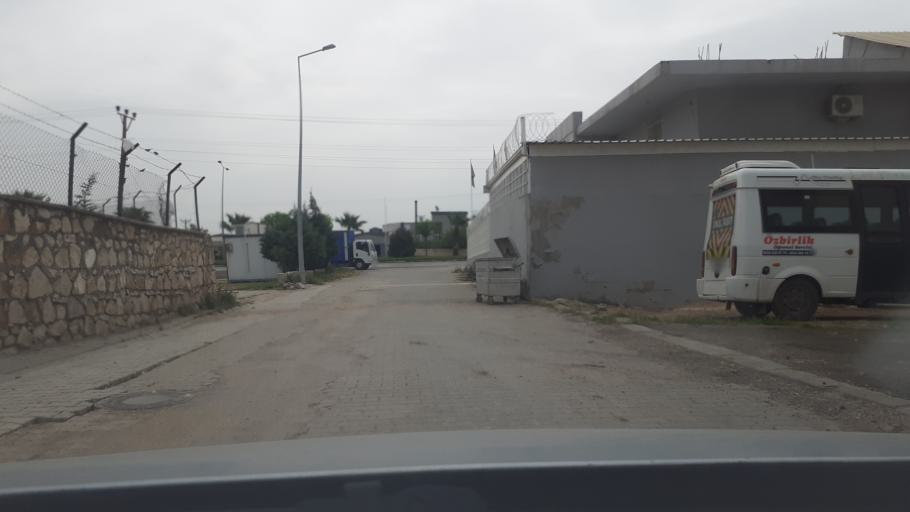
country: TR
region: Hatay
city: Kirikhan
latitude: 36.4916
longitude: 36.3692
